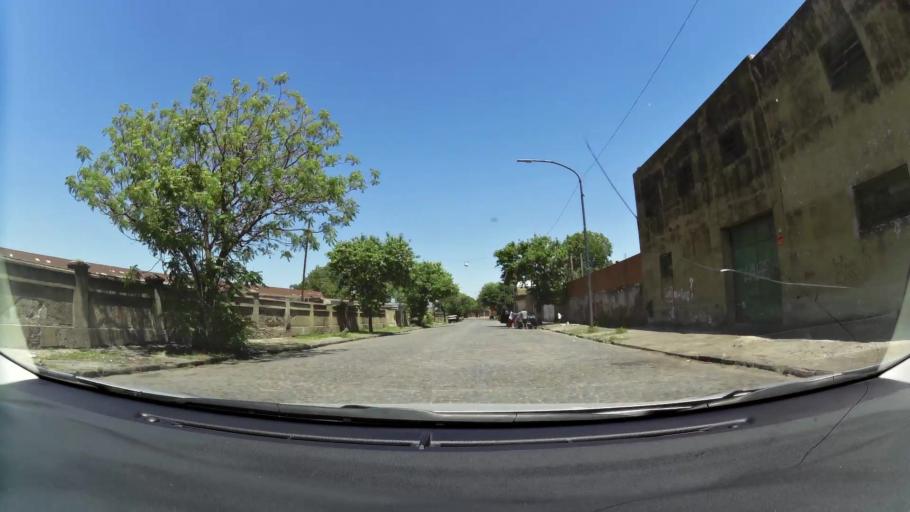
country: AR
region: Buenos Aires
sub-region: Partido de Avellaneda
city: Avellaneda
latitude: -34.6445
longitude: -58.3875
